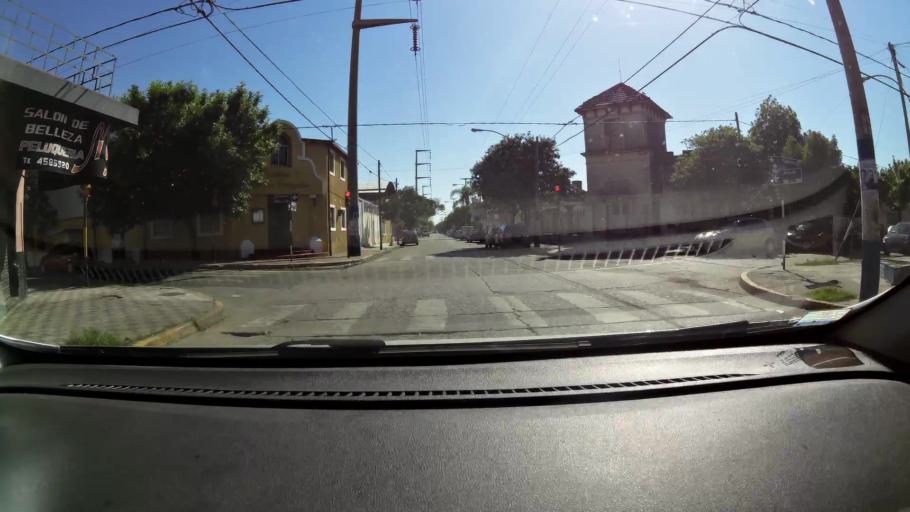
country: AR
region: Cordoba
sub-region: Departamento de Capital
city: Cordoba
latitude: -31.4388
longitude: -64.1582
